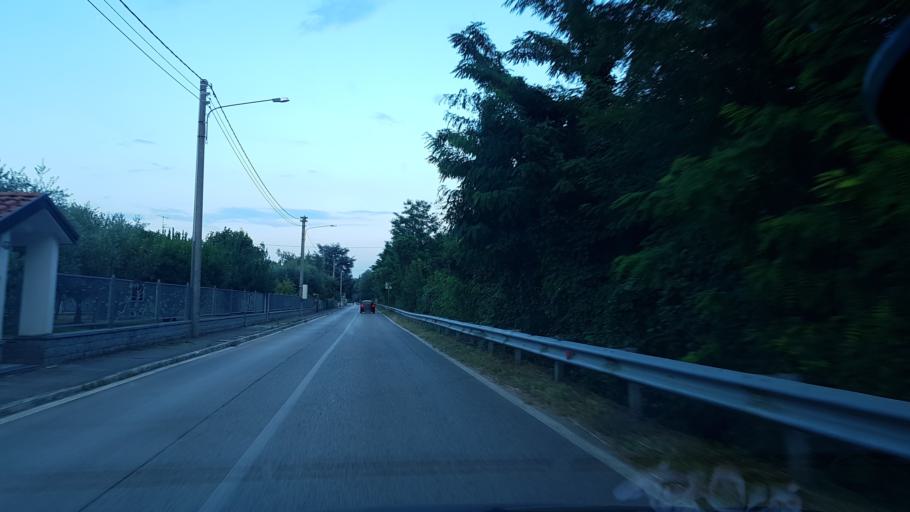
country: IT
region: Friuli Venezia Giulia
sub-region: Provincia di Gorizia
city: Capriva del Friuli
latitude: 45.9386
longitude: 13.5206
